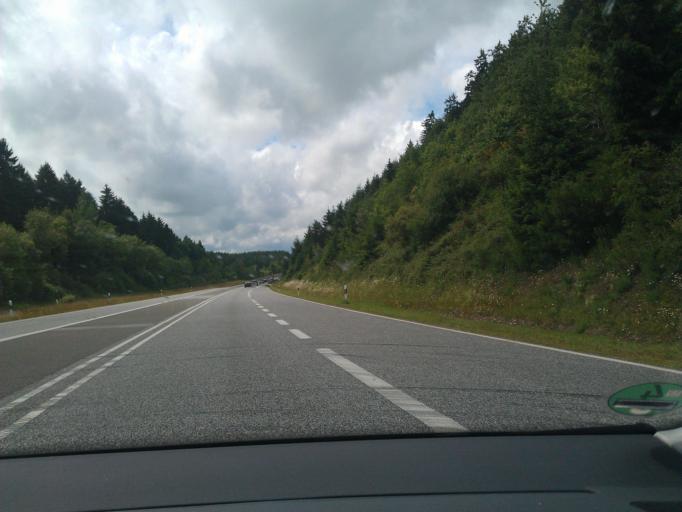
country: DE
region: Rheinland-Pfalz
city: Pittenbach
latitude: 50.2037
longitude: 6.3373
